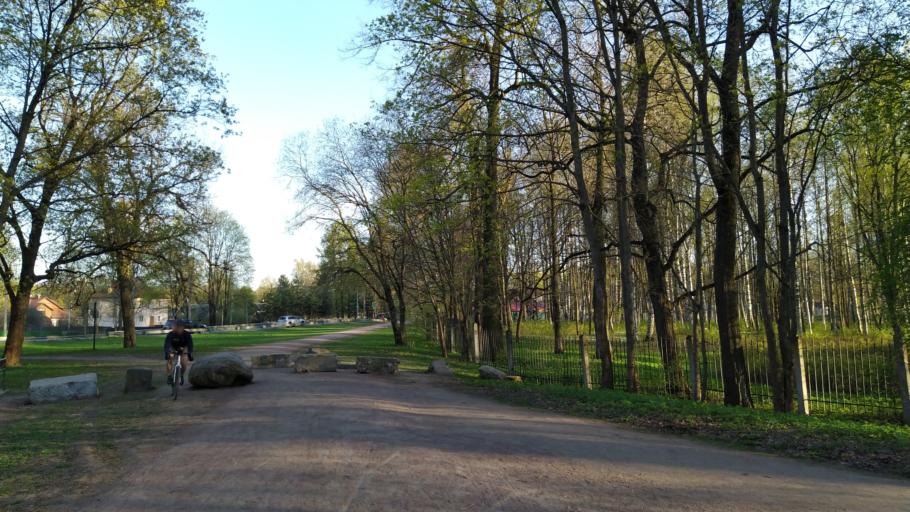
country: RU
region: St.-Petersburg
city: Pavlovsk
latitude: 59.6981
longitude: 30.4287
